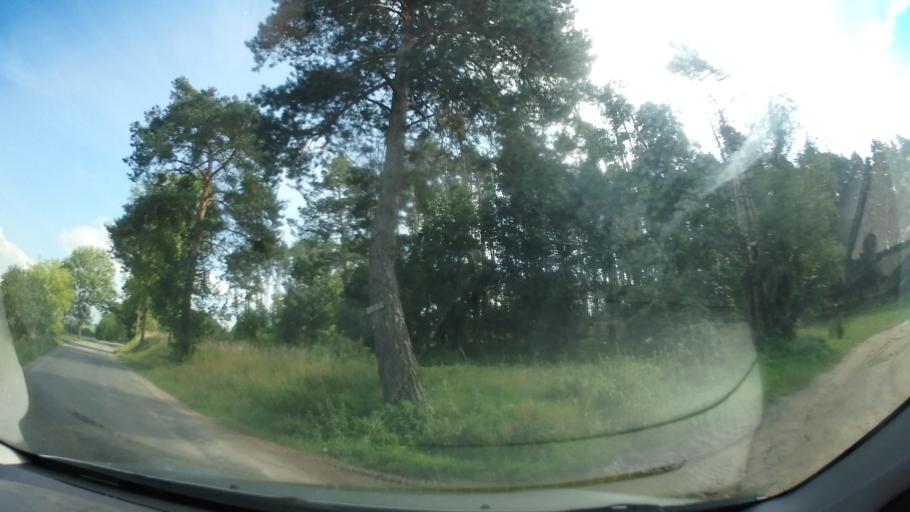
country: CZ
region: Central Bohemia
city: Novy Knin
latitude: 49.6968
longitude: 14.3198
